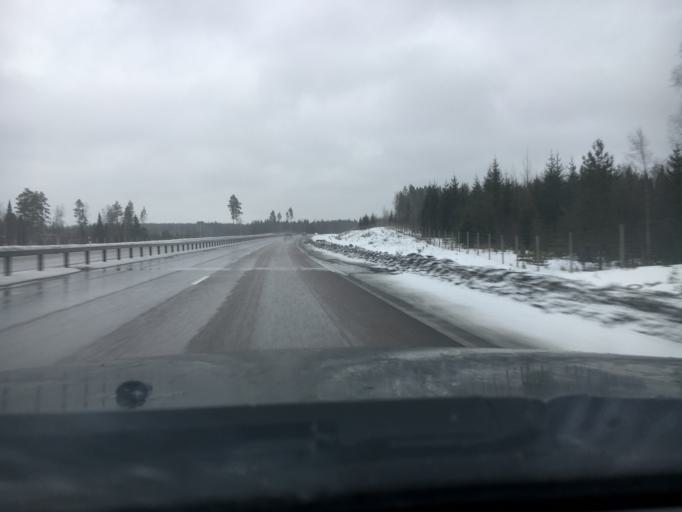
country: FI
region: Central Finland
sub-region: Joutsa
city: Joutsa
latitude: 61.8092
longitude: 26.0924
